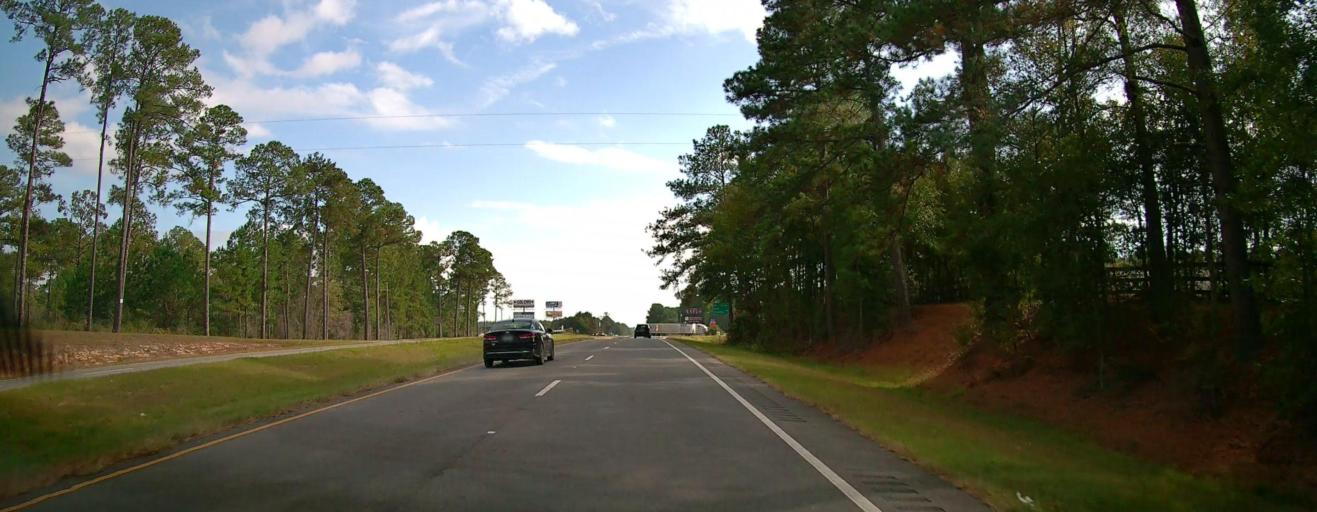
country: US
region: Georgia
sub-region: Thomas County
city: Meigs
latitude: 30.9795
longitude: -84.0383
